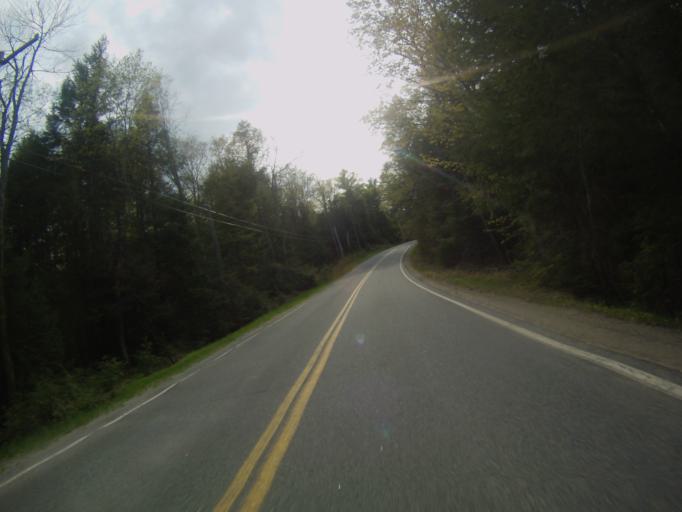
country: US
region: New York
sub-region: Warren County
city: Warrensburg
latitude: 43.8354
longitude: -73.8900
